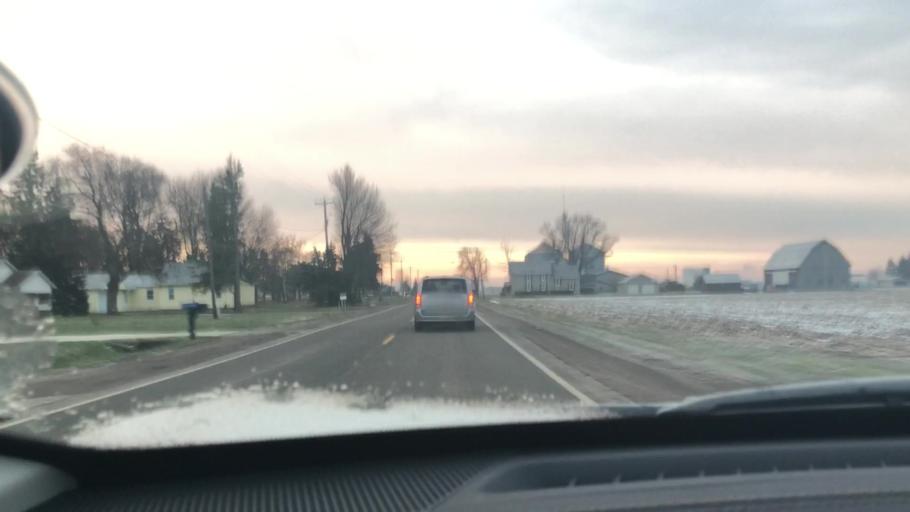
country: US
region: Michigan
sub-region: Saginaw County
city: Buena Vista
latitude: 43.4676
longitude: -83.8372
